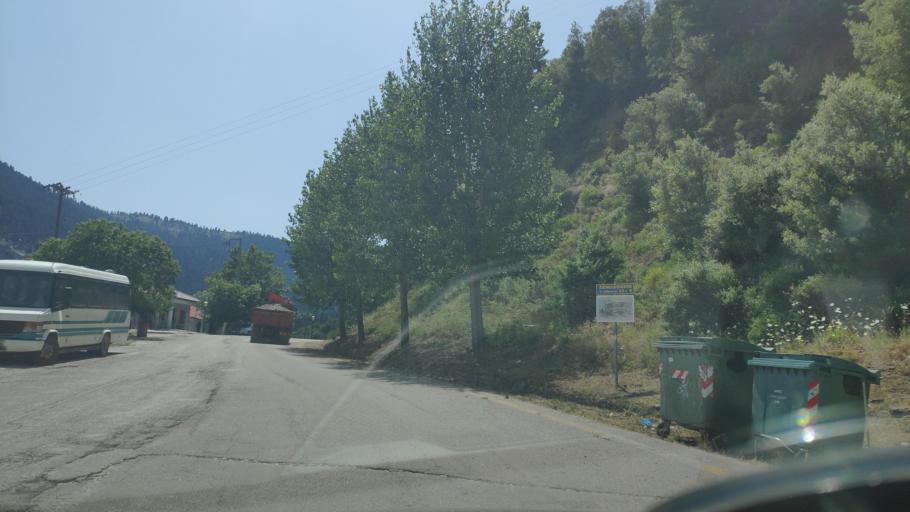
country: GR
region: Epirus
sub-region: Nomos Artas
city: Ano Kalentini
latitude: 39.2729
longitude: 21.2878
